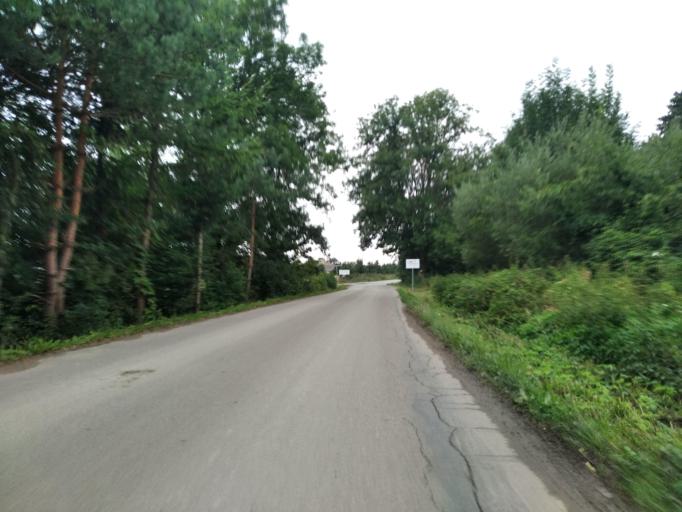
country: PL
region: Subcarpathian Voivodeship
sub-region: Powiat brzozowski
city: Dydnia
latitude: 49.6759
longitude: 22.2727
